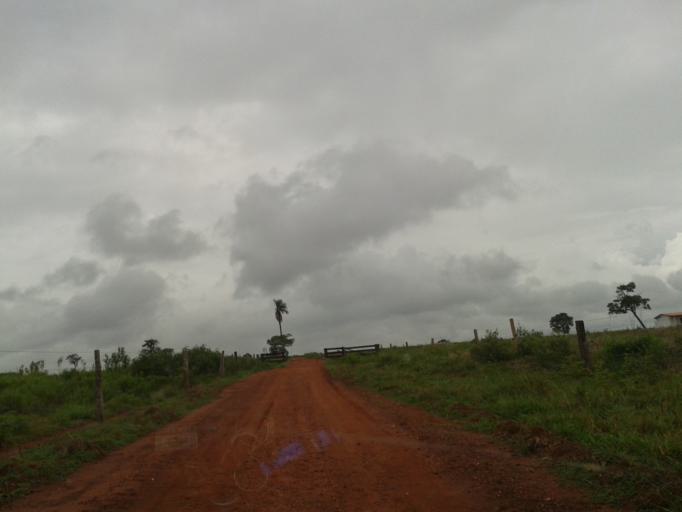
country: BR
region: Minas Gerais
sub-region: Santa Vitoria
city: Santa Vitoria
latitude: -18.7278
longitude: -49.9764
